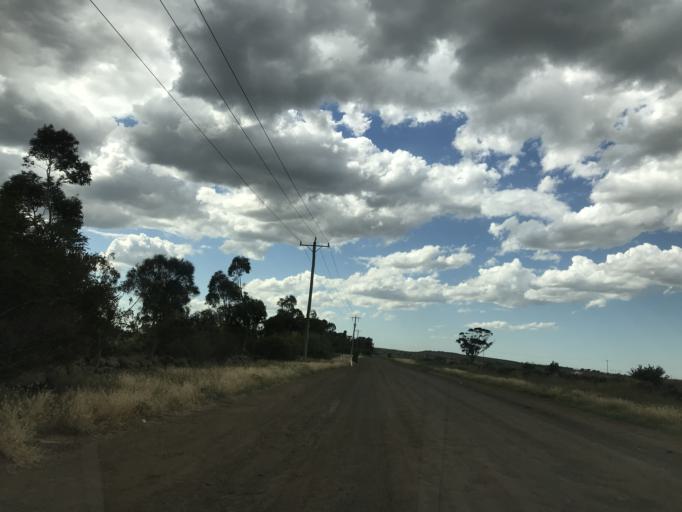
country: AU
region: Victoria
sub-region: Wyndham
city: Truganina
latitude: -37.8116
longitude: 144.7228
